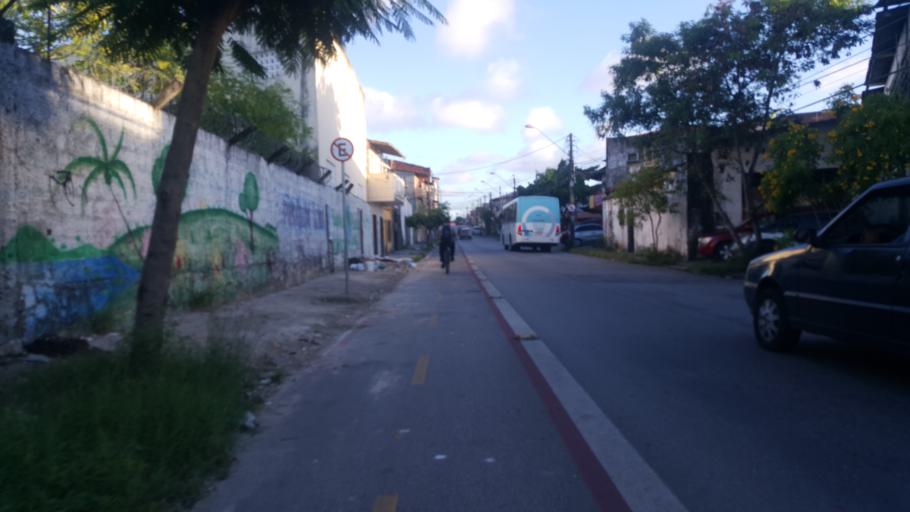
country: BR
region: Ceara
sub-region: Fortaleza
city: Fortaleza
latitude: -3.7498
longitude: -38.5394
